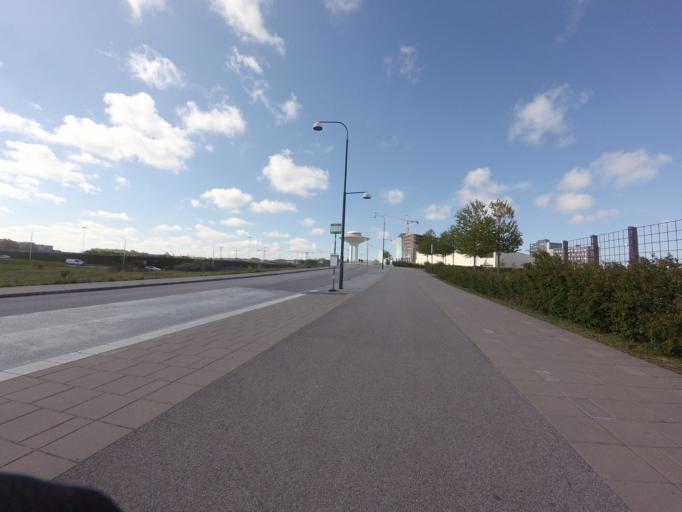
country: SE
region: Skane
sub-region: Malmo
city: Malmoe
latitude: 55.5692
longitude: 12.9806
